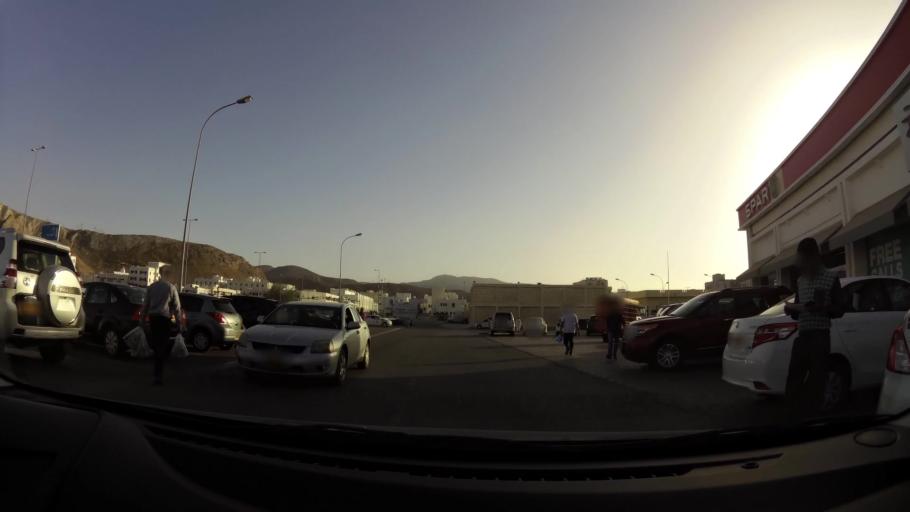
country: OM
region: Muhafazat Masqat
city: Muscat
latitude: 23.5895
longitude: 58.5531
